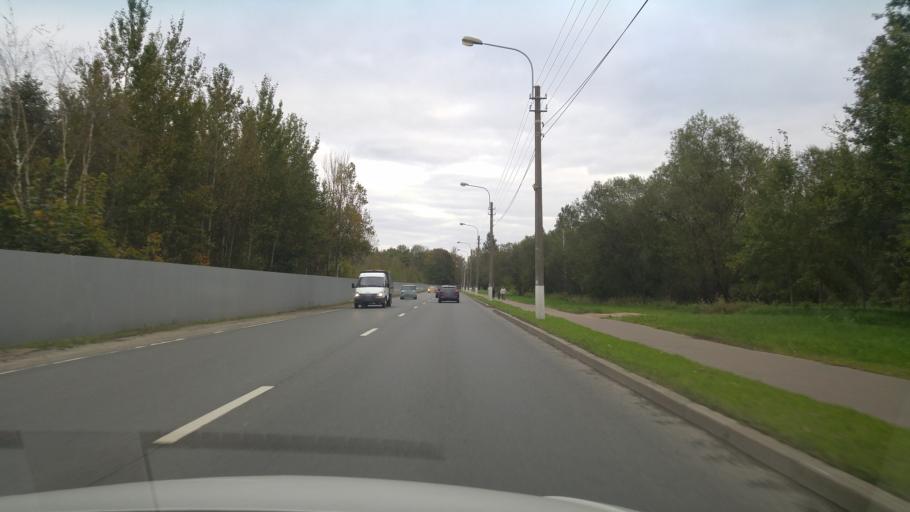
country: RU
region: St.-Petersburg
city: Kronshtadt
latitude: 60.0061
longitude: 29.7447
